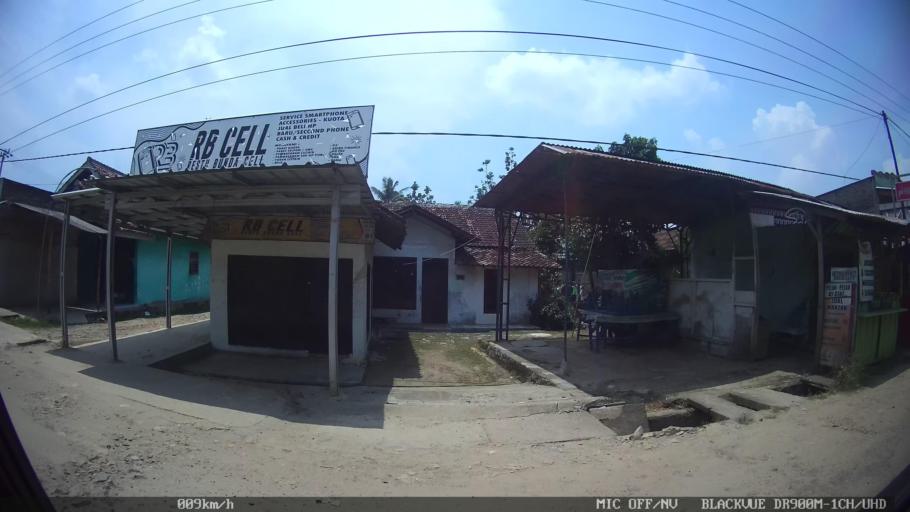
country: ID
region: Lampung
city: Natar
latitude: -5.3165
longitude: 105.2004
